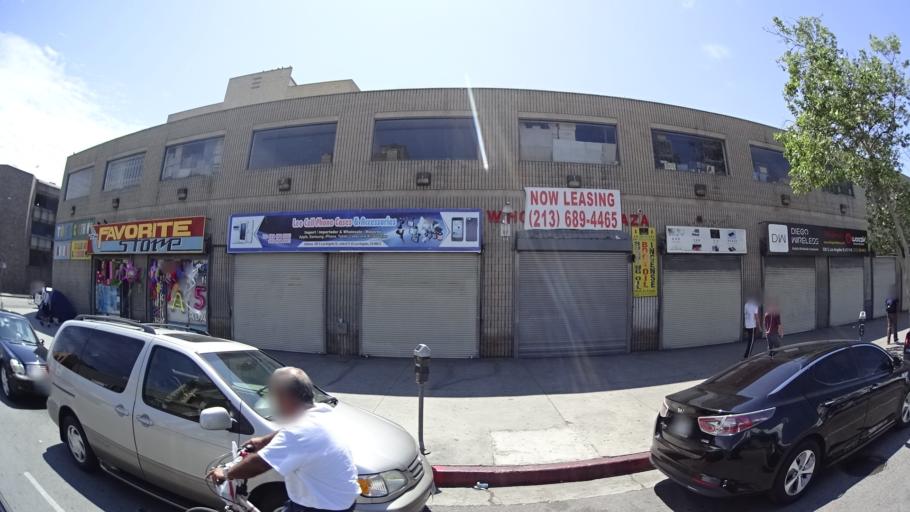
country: US
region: California
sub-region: Los Angeles County
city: Los Angeles
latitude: 34.0456
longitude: -118.2469
